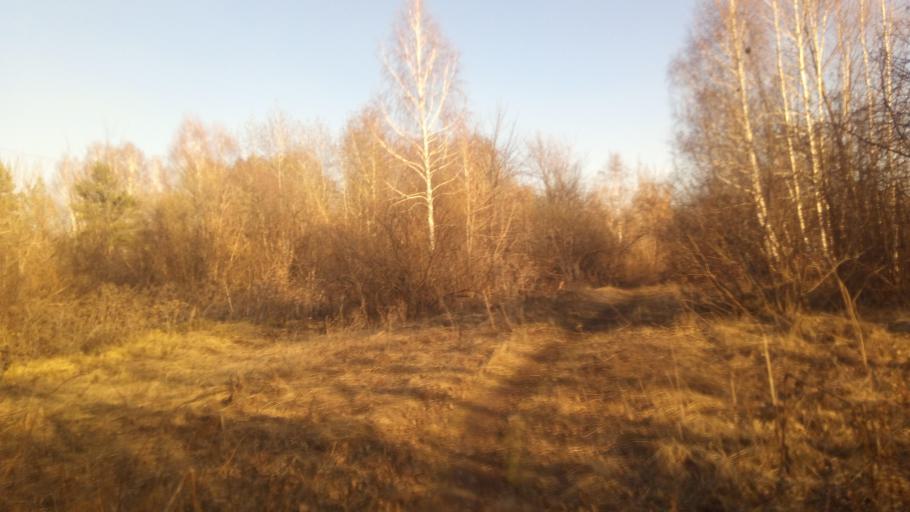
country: RU
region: Chelyabinsk
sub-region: Gorod Chelyabinsk
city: Chelyabinsk
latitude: 55.1515
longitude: 61.3233
